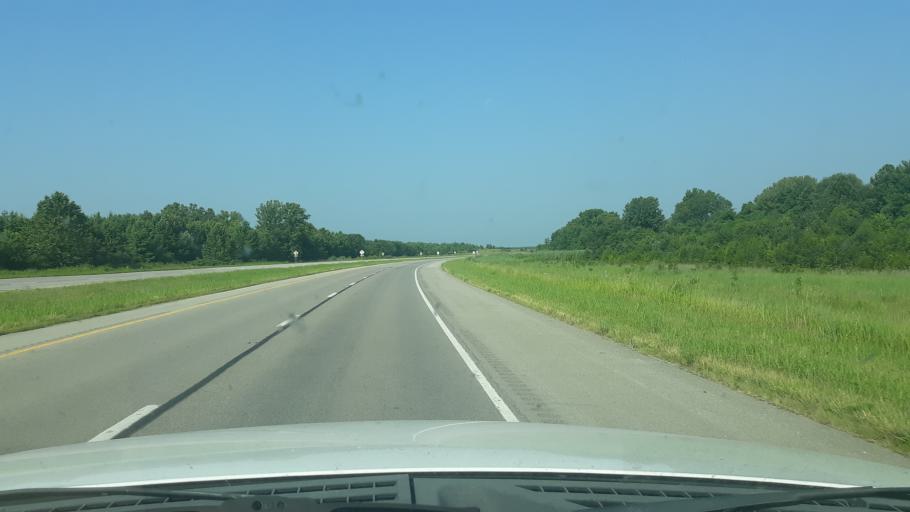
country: US
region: Illinois
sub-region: Saline County
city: Harrisburg
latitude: 37.7344
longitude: -88.5703
